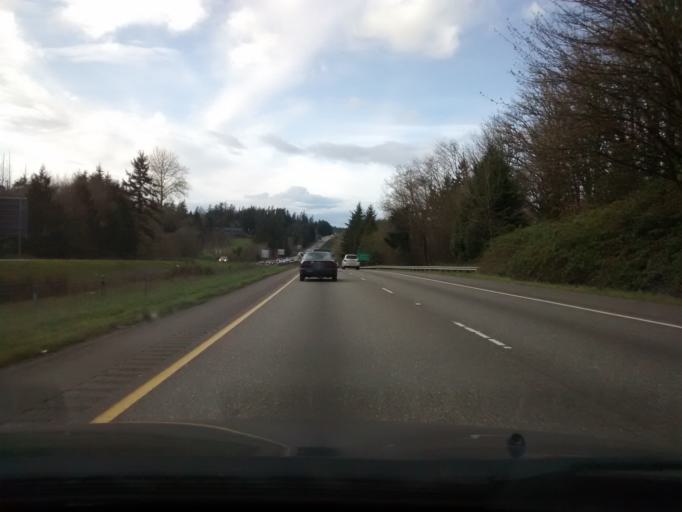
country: US
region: Washington
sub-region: Pierce County
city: Gig Harbor
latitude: 47.3268
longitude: -122.5955
